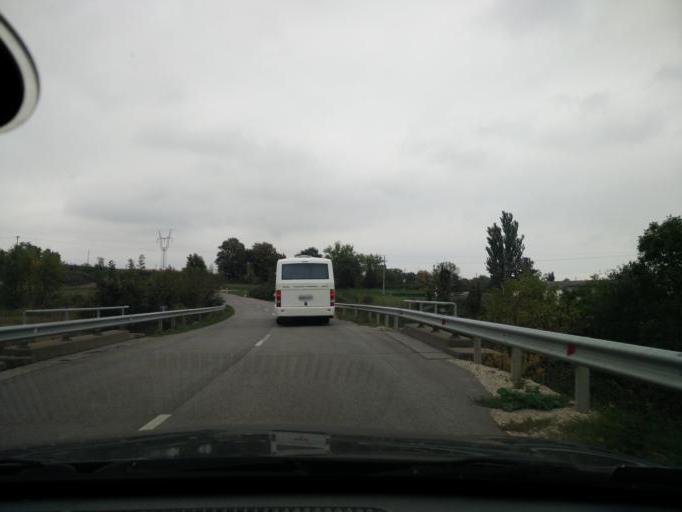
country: HU
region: Komarom-Esztergom
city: Bajna
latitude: 47.6801
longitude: 18.6125
